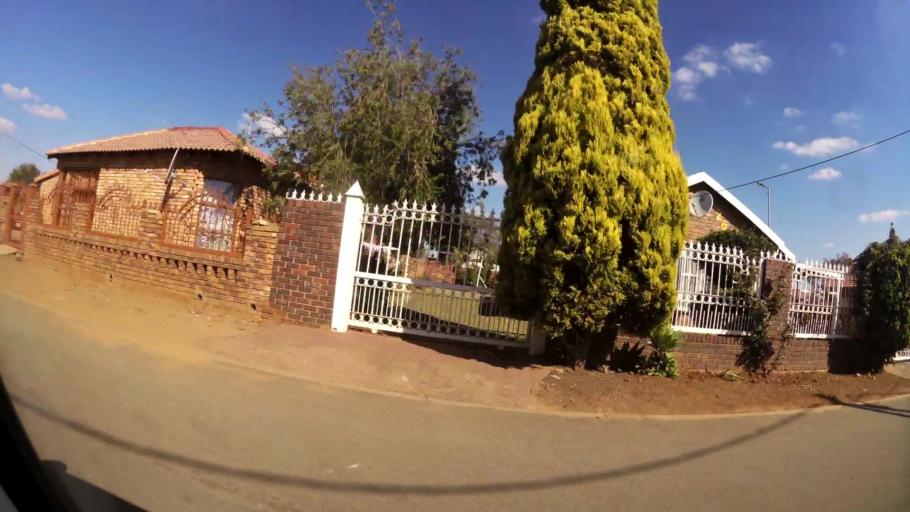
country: ZA
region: Gauteng
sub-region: City of Tshwane Metropolitan Municipality
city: Cullinan
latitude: -25.7174
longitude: 28.4013
